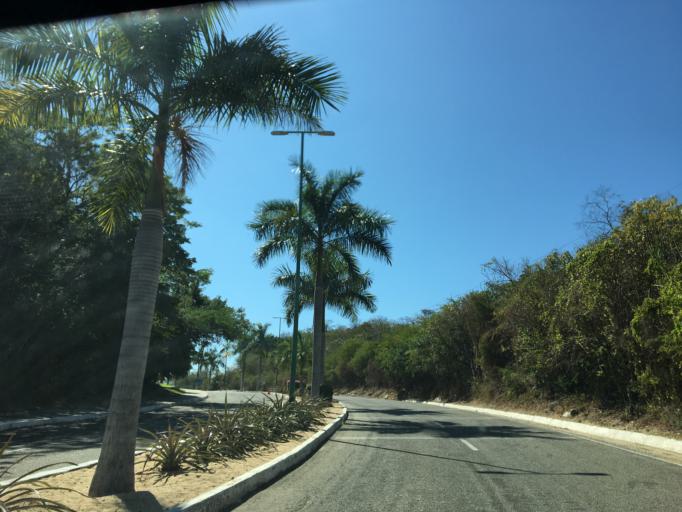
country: MX
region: Oaxaca
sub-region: Santa Maria Huatulco
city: Crucecita
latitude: 15.7839
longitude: -96.0665
